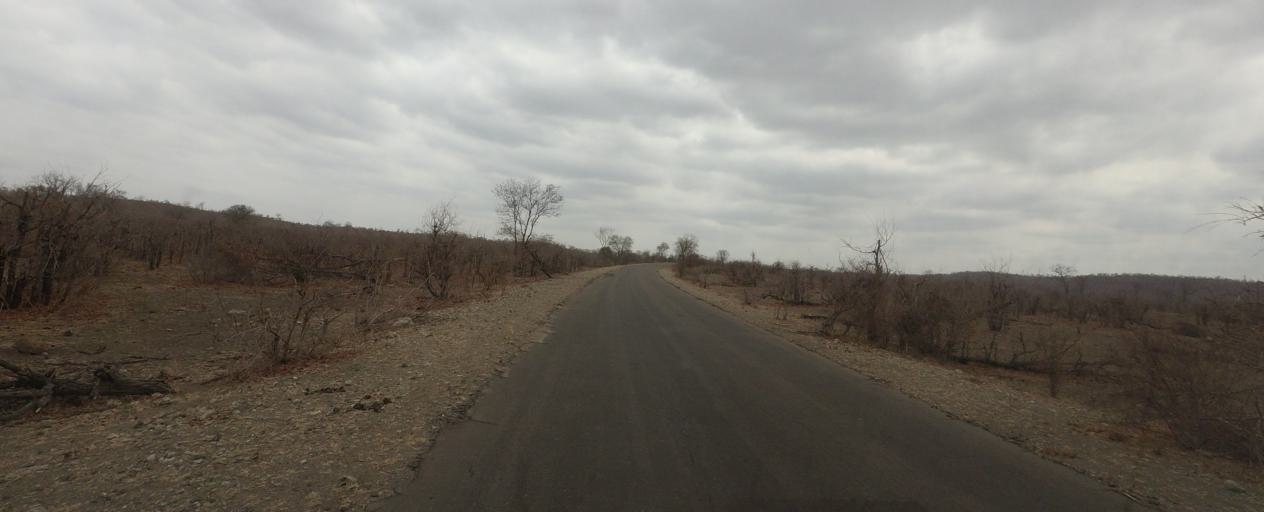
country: ZA
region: Limpopo
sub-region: Vhembe District Municipality
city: Mutale
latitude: -22.4063
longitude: 31.2103
